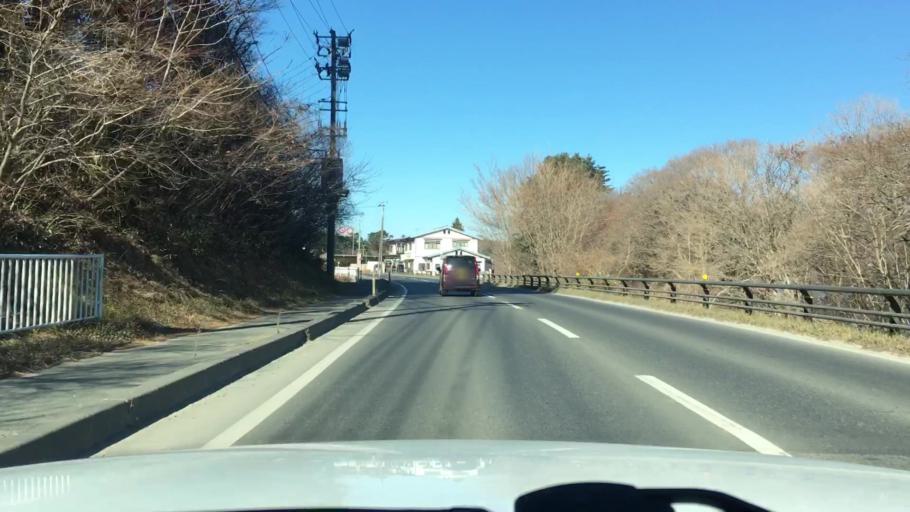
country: JP
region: Iwate
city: Yamada
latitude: 39.4419
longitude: 141.9717
